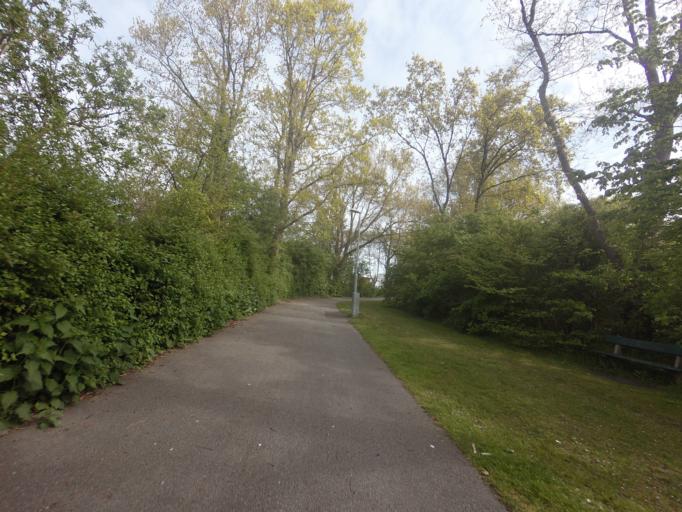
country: SE
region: Skane
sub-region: Hoganas Kommun
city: Hoganas
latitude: 56.1933
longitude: 12.5799
